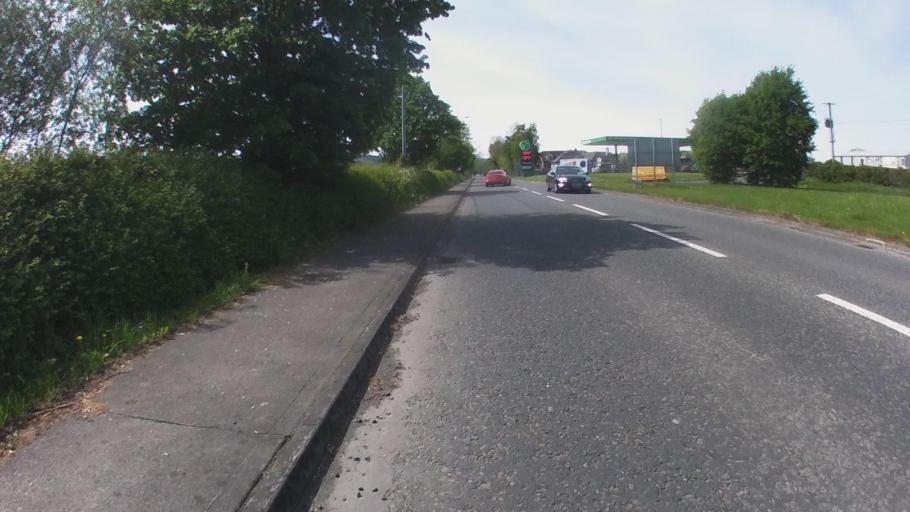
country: IE
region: Leinster
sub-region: County Carlow
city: Carlow
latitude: 52.8398
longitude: -6.9576
